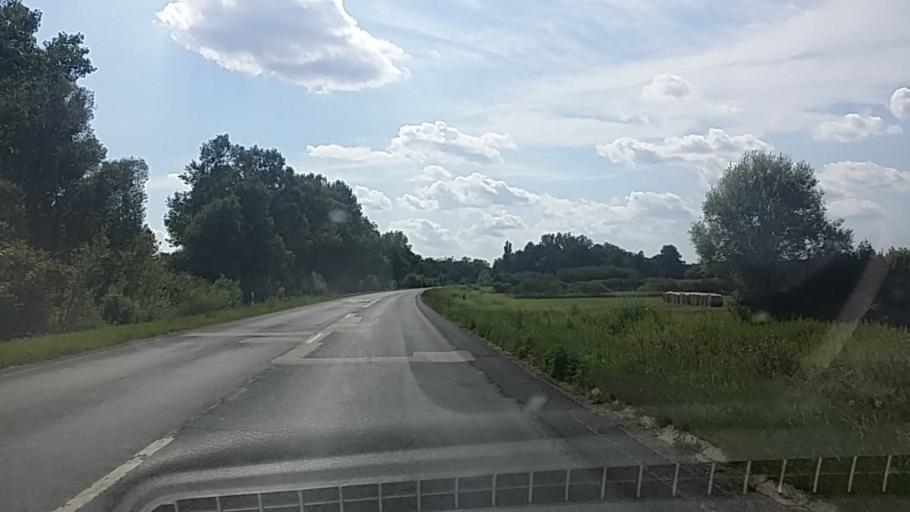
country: HU
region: Zala
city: Nagykanizsa
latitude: 46.4616
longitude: 16.9402
